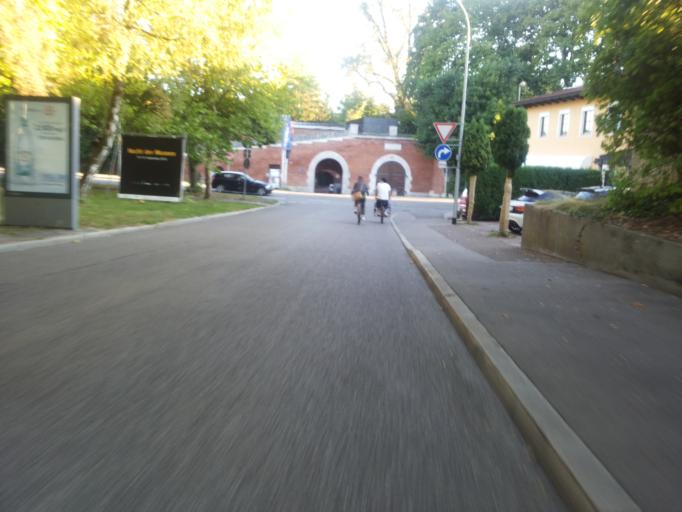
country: DE
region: Bavaria
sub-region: Upper Bavaria
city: Ingolstadt
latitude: 48.7648
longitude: 11.4164
